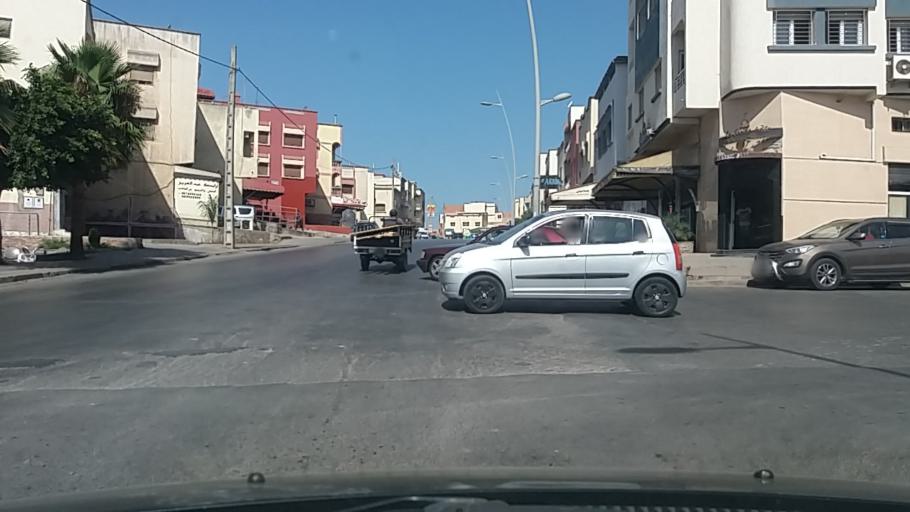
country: MA
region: Gharb-Chrarda-Beni Hssen
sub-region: Kenitra Province
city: Kenitra
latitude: 34.2657
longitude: -6.6135
